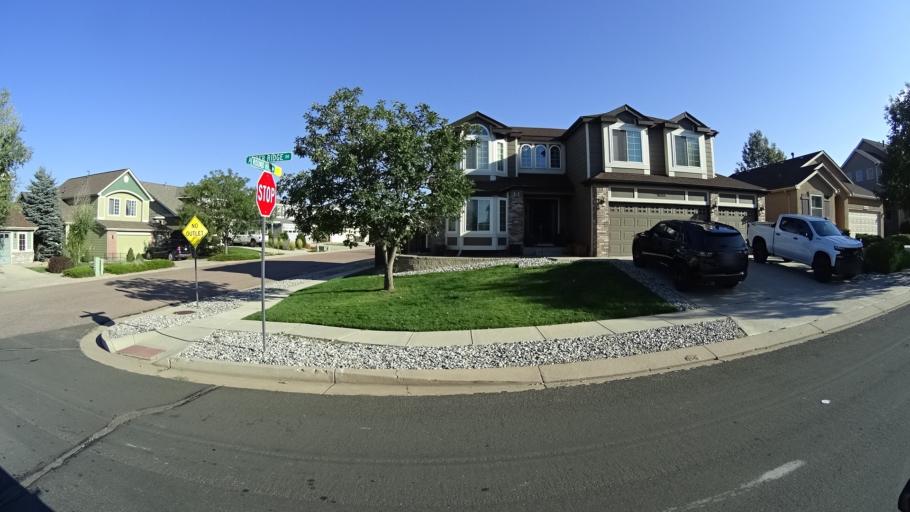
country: US
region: Colorado
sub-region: El Paso County
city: Cimarron Hills
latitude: 38.8941
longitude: -104.7011
